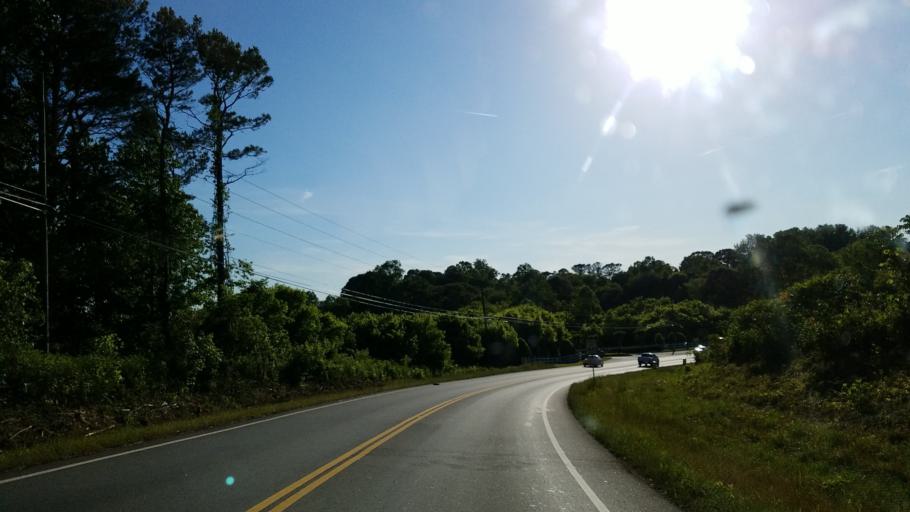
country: US
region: Georgia
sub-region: Cherokee County
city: Holly Springs
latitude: 34.1658
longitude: -84.4337
